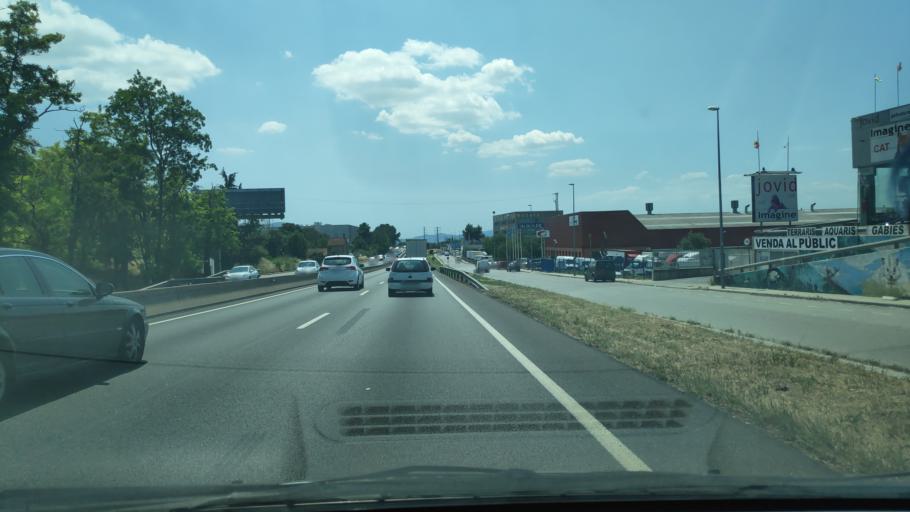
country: ES
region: Catalonia
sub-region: Provincia de Barcelona
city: Llica de Vall
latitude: 41.5781
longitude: 2.2516
